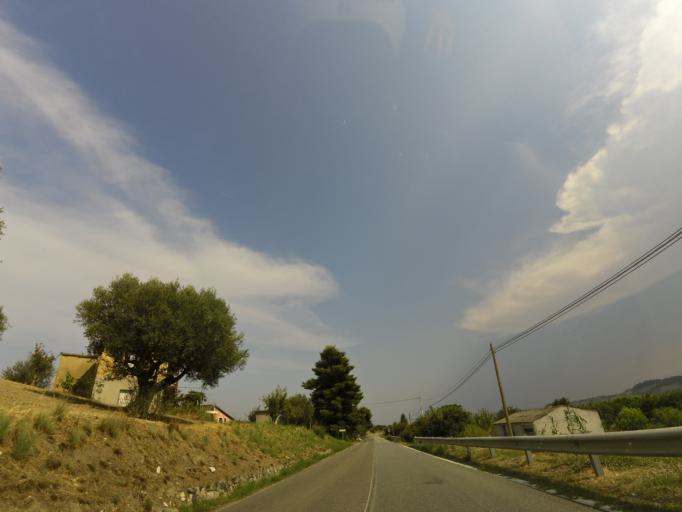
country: IT
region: Calabria
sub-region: Provincia di Reggio Calabria
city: Monasterace
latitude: 38.4496
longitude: 16.5317
